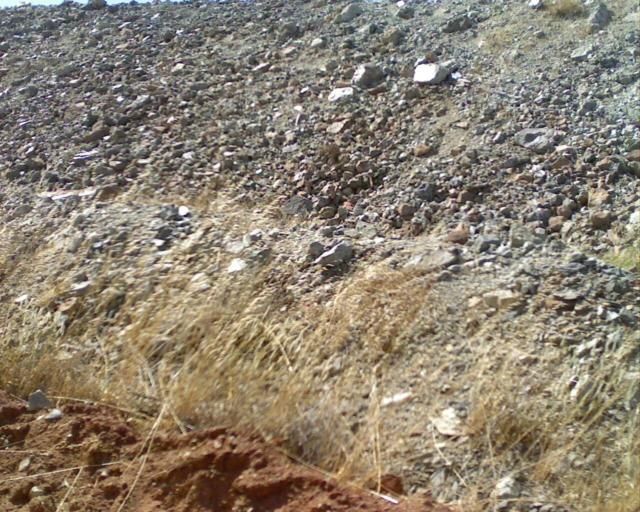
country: AU
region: Western Australia
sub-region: Irwin
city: Dongara
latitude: -29.4960
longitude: 115.8594
